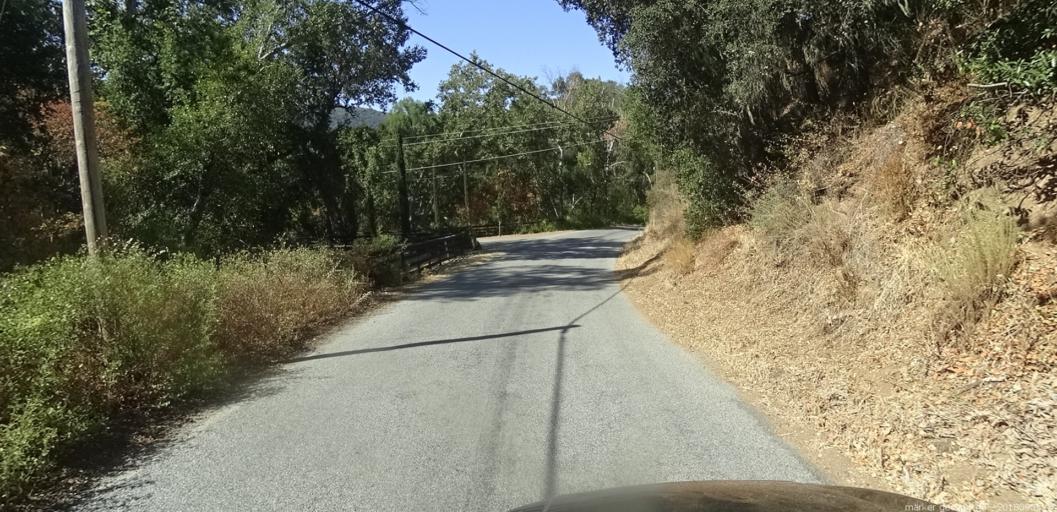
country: US
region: California
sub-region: Monterey County
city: Carmel Valley Village
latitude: 36.3915
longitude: -121.6284
